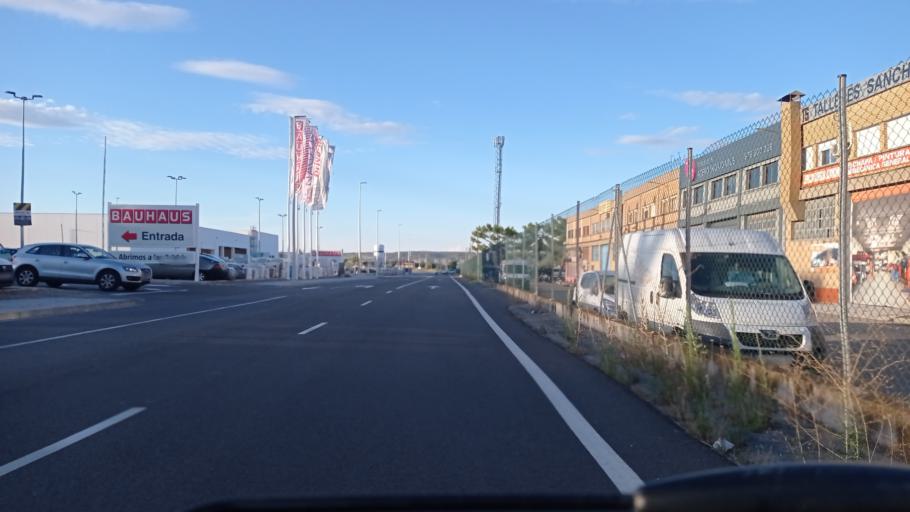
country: ES
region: Aragon
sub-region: Provincia de Zaragoza
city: Oliver-Valdefierro, Oliver, Valdefierro
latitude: 41.6746
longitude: -0.9502
